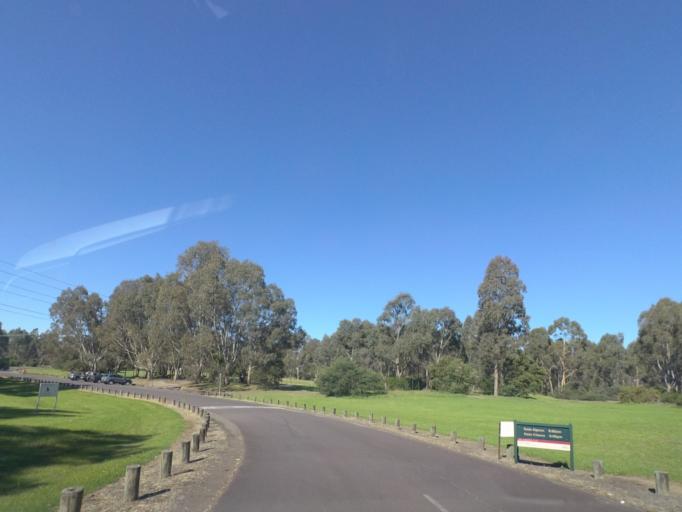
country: AU
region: Victoria
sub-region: Banyule
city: Viewbank
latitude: -37.7549
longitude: 145.0959
